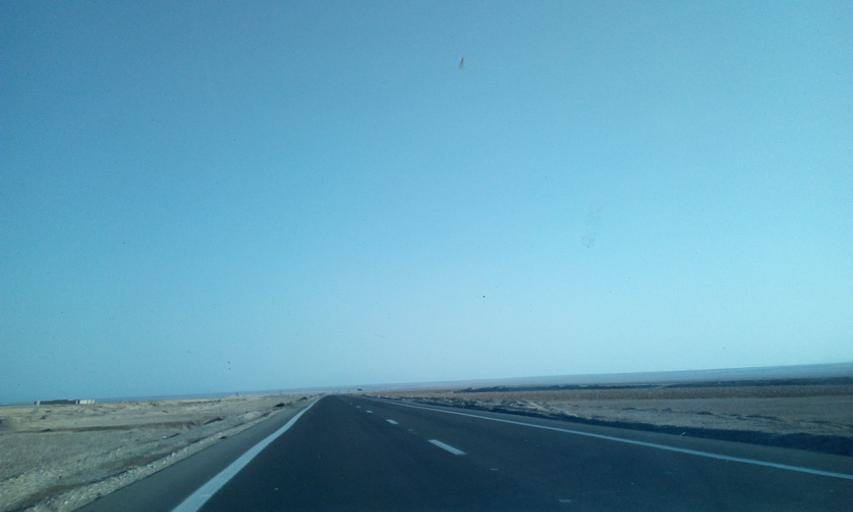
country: EG
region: South Sinai
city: Tor
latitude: 28.6203
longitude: 32.8603
